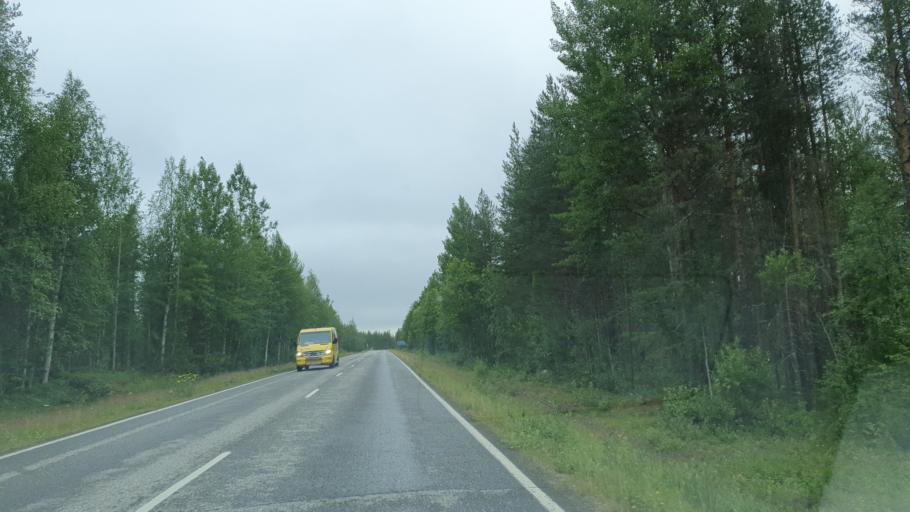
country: FI
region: Lapland
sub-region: Itae-Lappi
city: Pyhaejaervi
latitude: 67.2637
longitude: 27.2648
